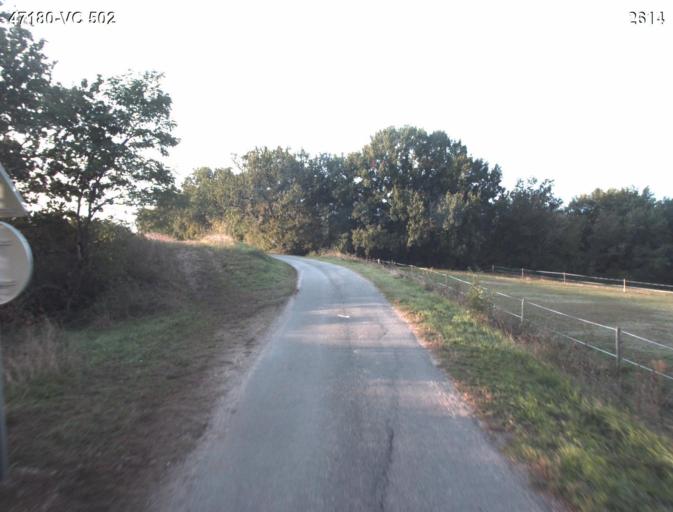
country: FR
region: Aquitaine
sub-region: Departement du Lot-et-Garonne
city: Sainte-Colombe-en-Bruilhois
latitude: 44.1802
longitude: 0.4828
